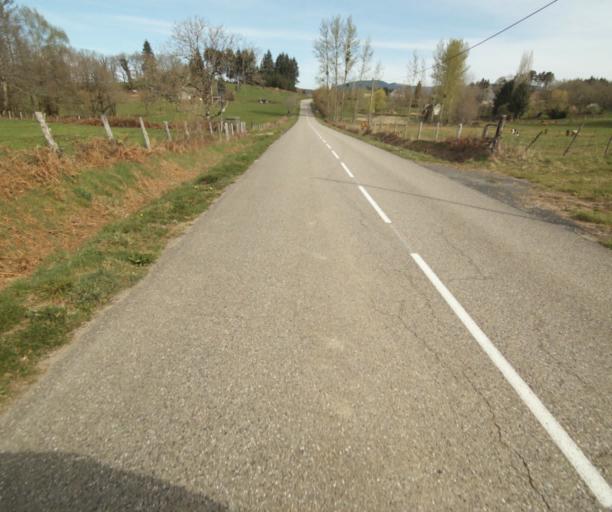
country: FR
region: Limousin
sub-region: Departement de la Correze
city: Correze
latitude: 45.4091
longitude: 1.8266
